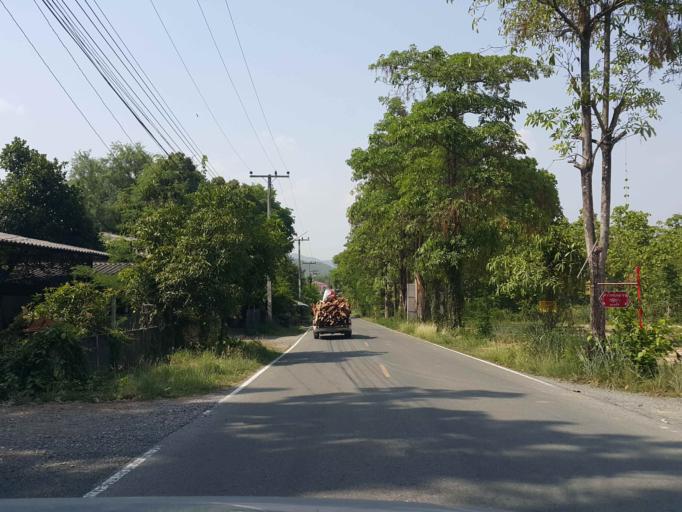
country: TH
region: Chiang Mai
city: Mae On
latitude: 18.8187
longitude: 99.1779
